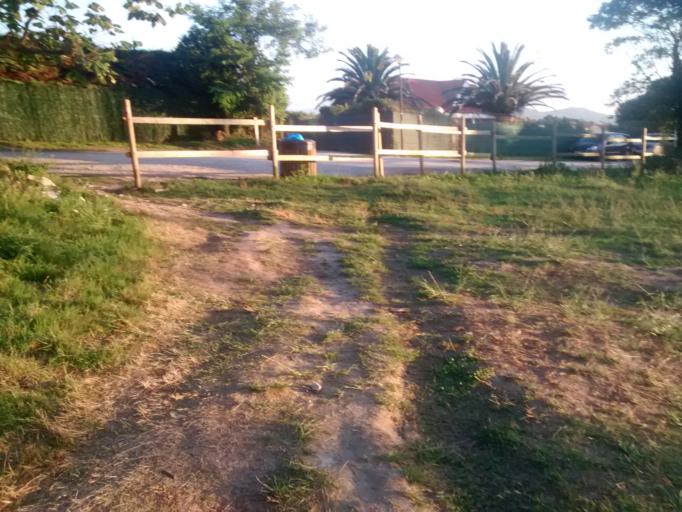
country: ES
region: Cantabria
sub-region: Provincia de Cantabria
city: Santander
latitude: 43.4560
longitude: -3.7366
